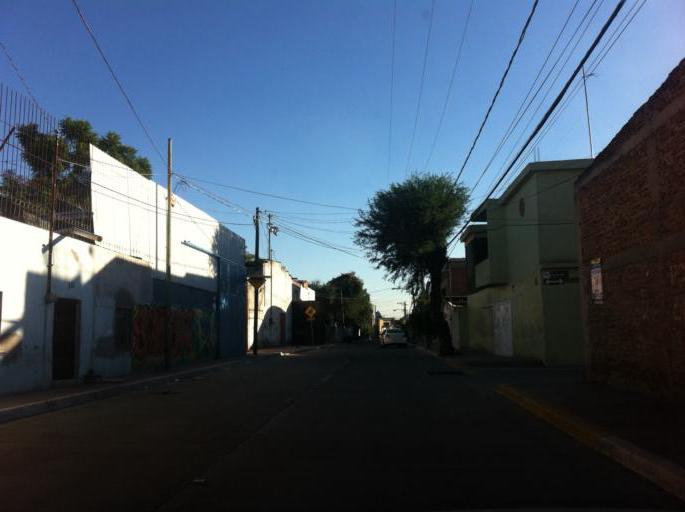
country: MX
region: Guanajuato
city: Leon
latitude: 21.1067
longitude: -101.6866
